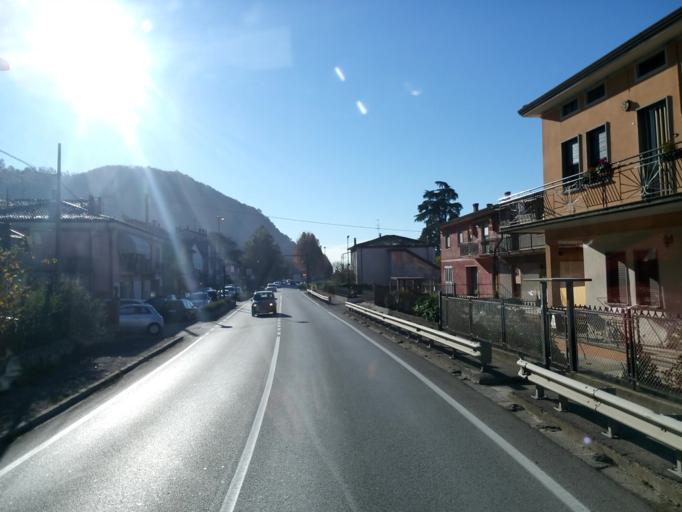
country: IT
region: Veneto
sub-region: Provincia di Vicenza
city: Tezze
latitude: 45.5388
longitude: 11.3848
